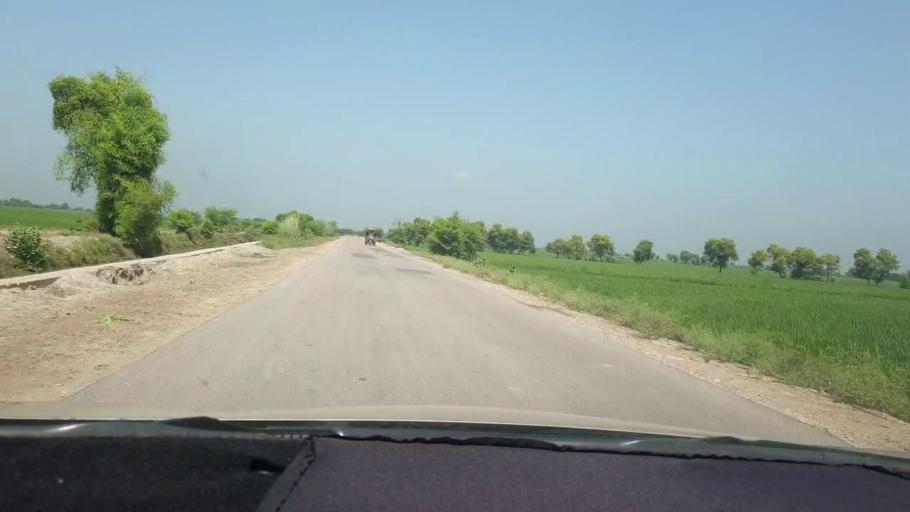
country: PK
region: Sindh
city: Miro Khan
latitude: 27.7595
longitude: 68.0793
